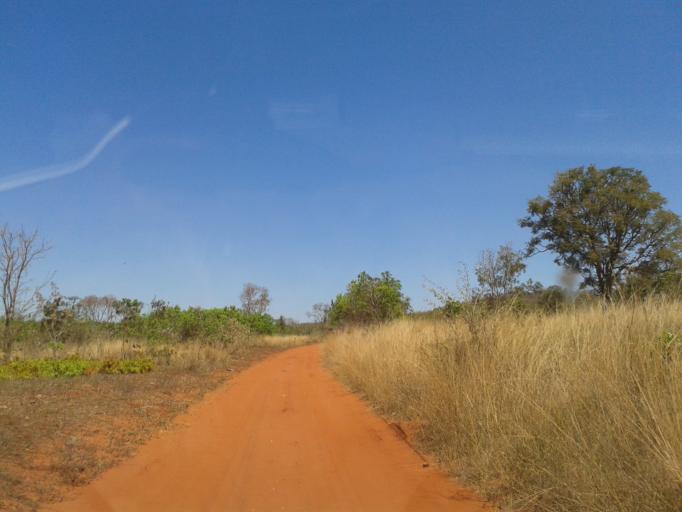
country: BR
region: Minas Gerais
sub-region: Ituiutaba
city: Ituiutaba
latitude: -19.1141
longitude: -49.2873
